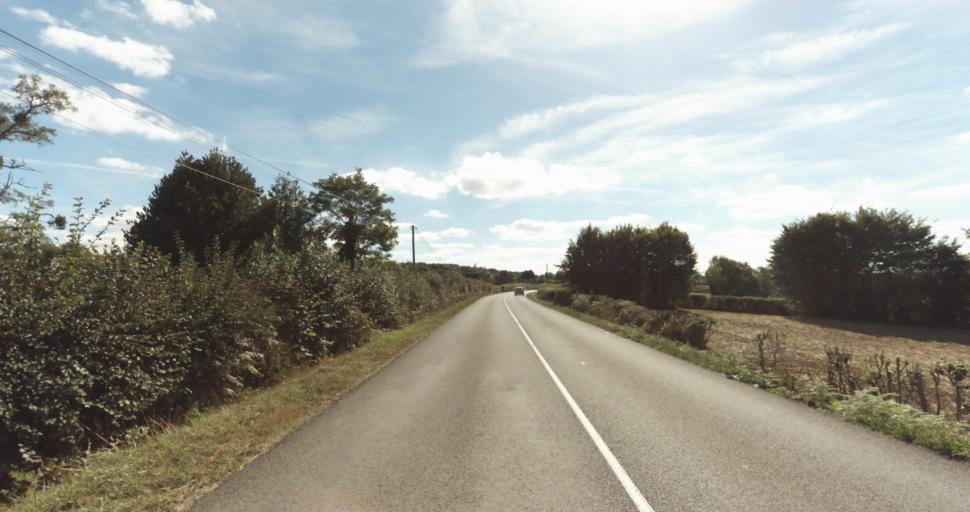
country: FR
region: Lower Normandy
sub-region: Departement de l'Orne
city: Vimoutiers
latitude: 48.9140
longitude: 0.1490
